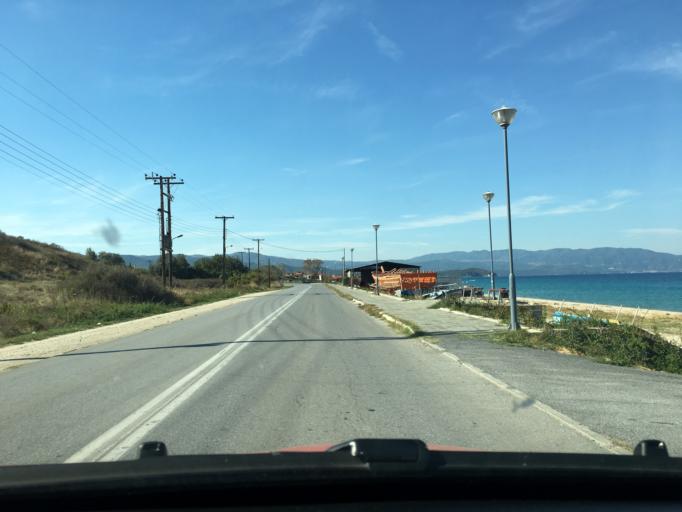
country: GR
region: Central Macedonia
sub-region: Nomos Chalkidikis
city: Ierissos
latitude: 40.3953
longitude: 23.8883
